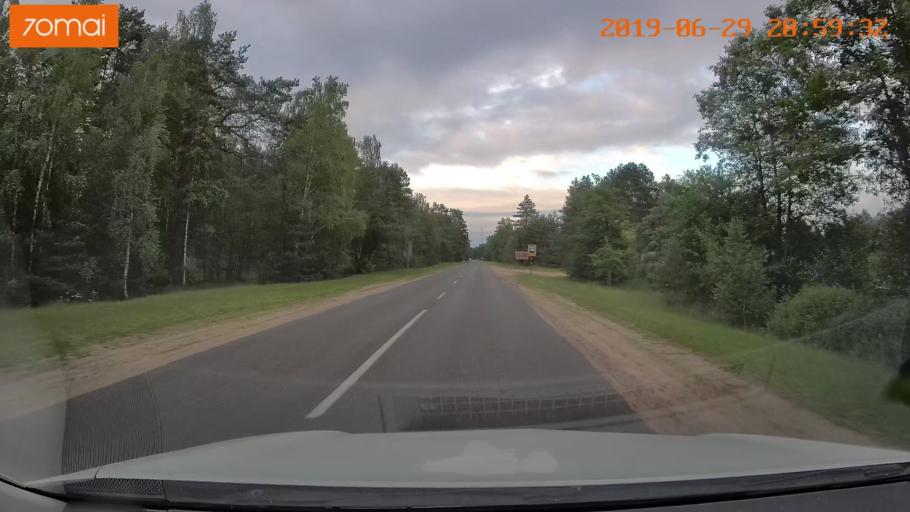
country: BY
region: Brest
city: Hantsavichy
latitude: 52.7376
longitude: 26.4080
